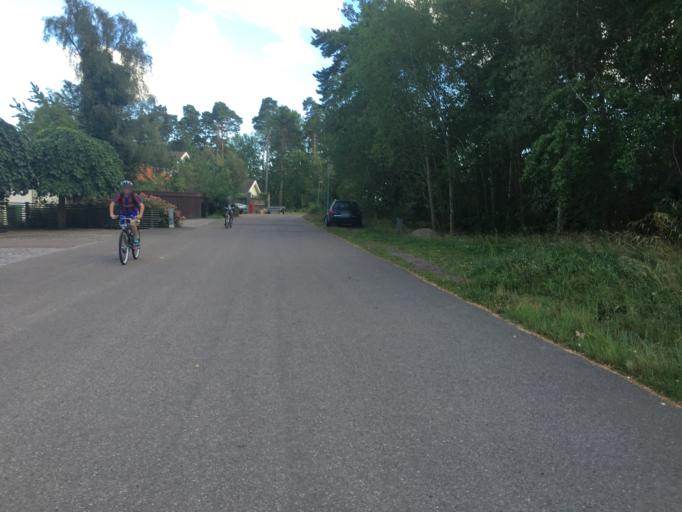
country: SE
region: Kalmar
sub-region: Kalmar Kommun
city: Kalmar
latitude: 56.7027
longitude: 16.3723
